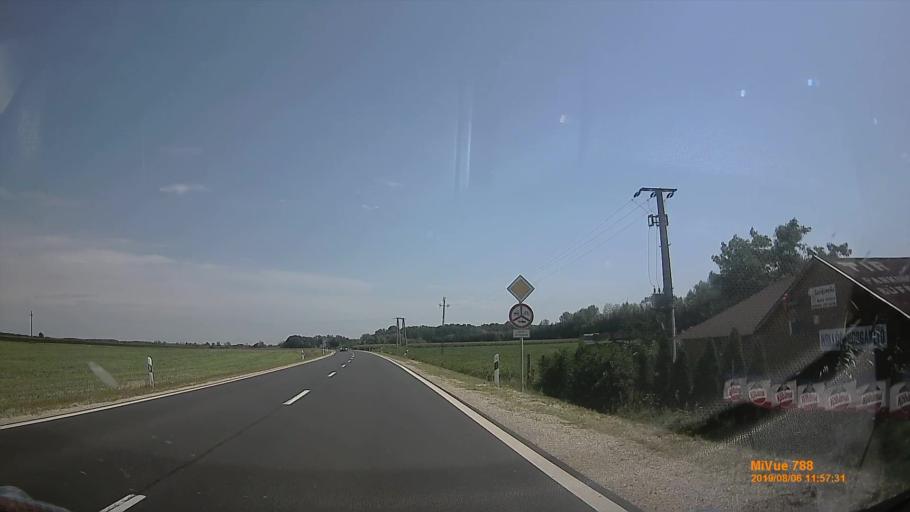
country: HU
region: Vas
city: Vasvar
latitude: 47.0598
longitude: 16.7110
